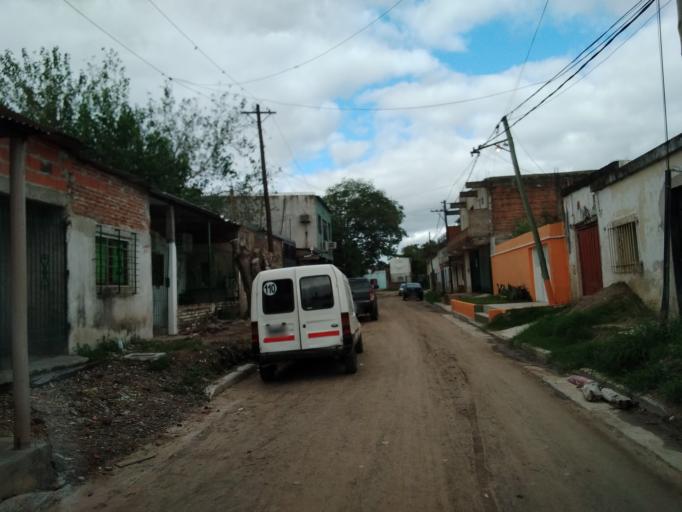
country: AR
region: Corrientes
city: Corrientes
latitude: -27.4738
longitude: -58.8084
